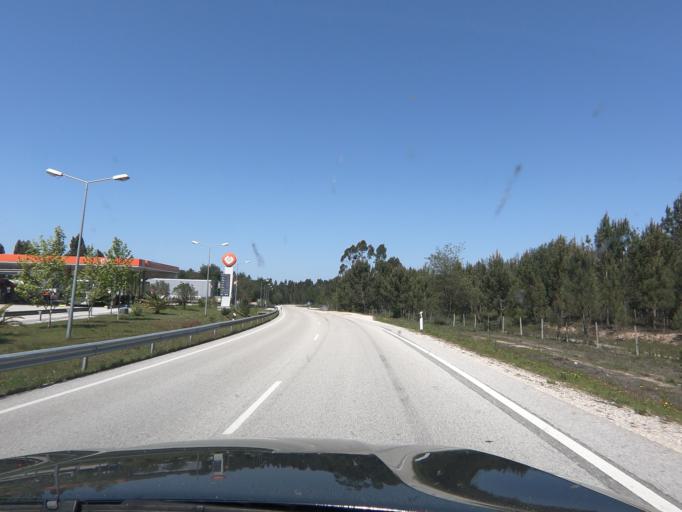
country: PT
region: Coimbra
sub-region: Lousa
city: Lousa
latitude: 40.1168
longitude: -8.2873
